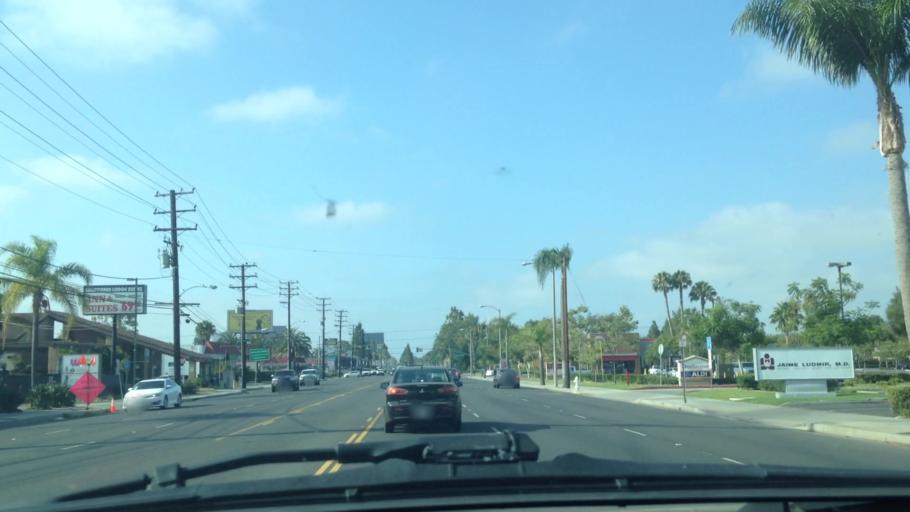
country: US
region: California
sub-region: Orange County
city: Santa Ana
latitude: 33.7095
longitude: -117.8855
